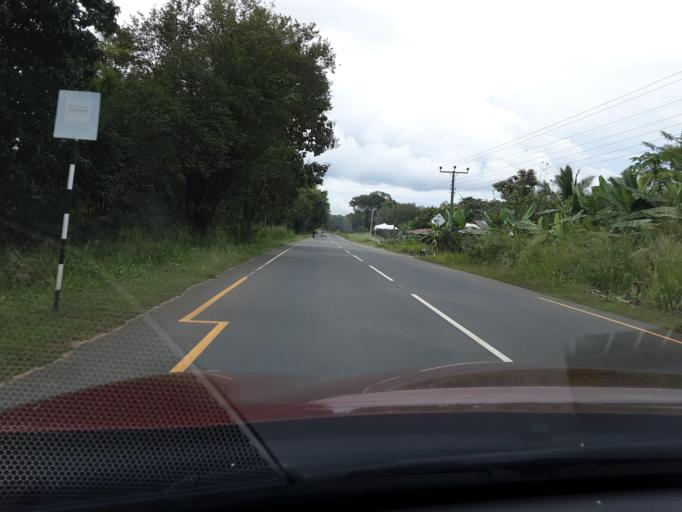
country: LK
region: Uva
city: Badulla
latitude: 7.3941
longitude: 81.1282
